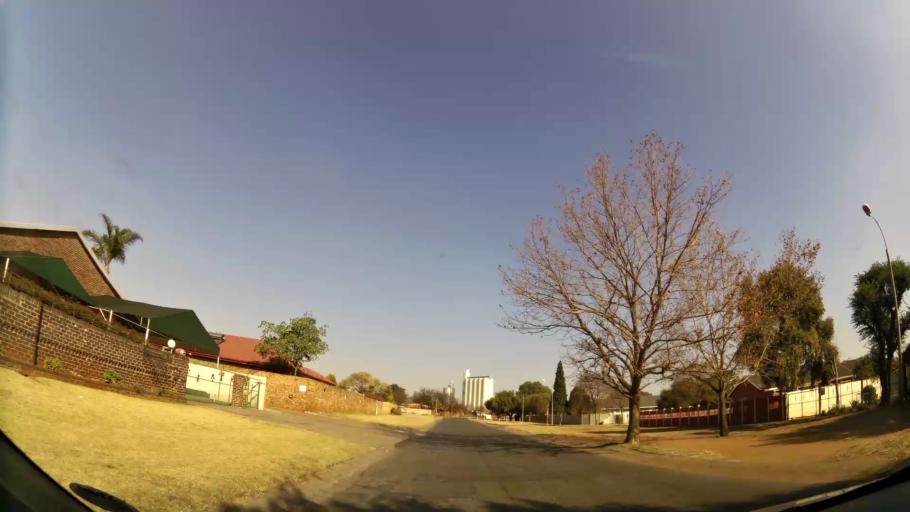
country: ZA
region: Gauteng
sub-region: West Rand District Municipality
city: Randfontein
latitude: -26.1798
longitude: 27.6925
